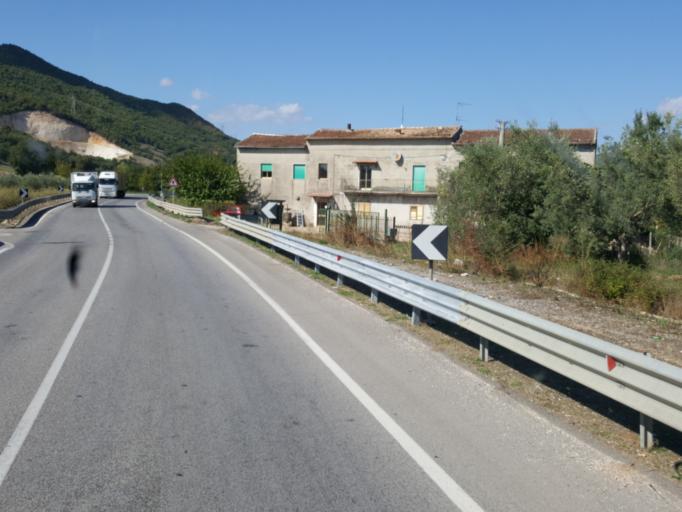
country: IT
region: Campania
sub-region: Provincia di Caserta
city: Presenzano
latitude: 41.3816
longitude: 14.1043
